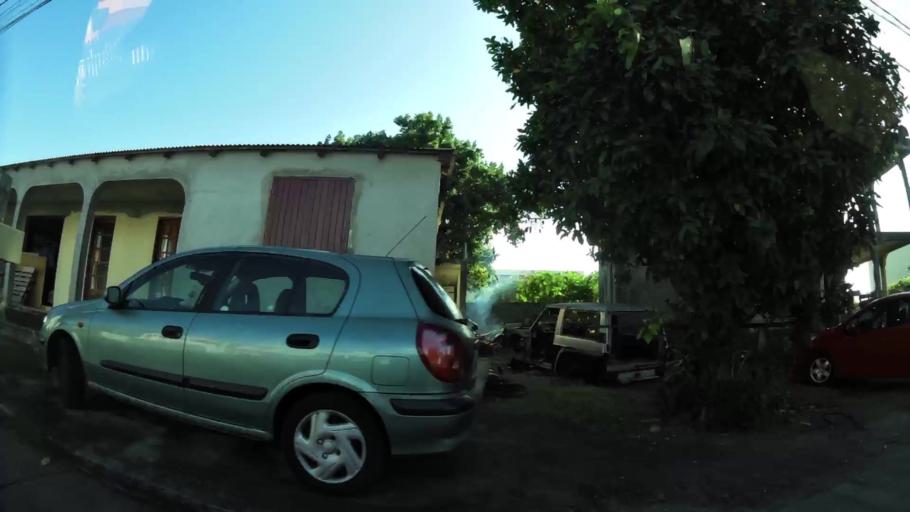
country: GP
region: Guadeloupe
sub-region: Guadeloupe
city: Le Gosier
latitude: 16.2032
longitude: -61.4773
